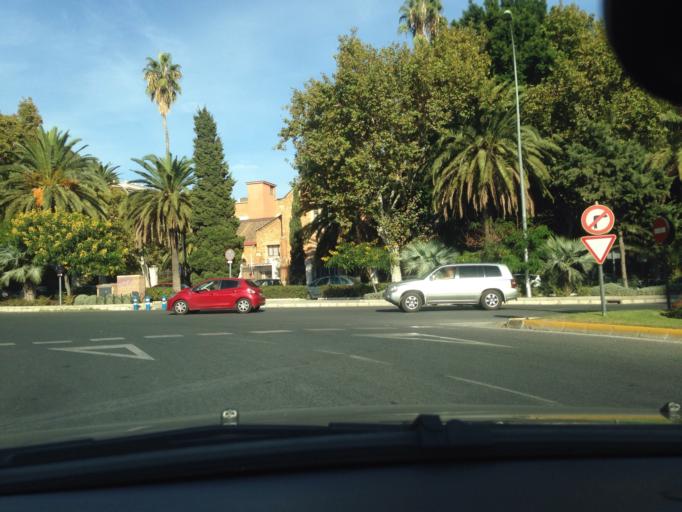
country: ES
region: Andalusia
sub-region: Provincia de Malaga
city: Malaga
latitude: 36.7202
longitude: -4.4125
